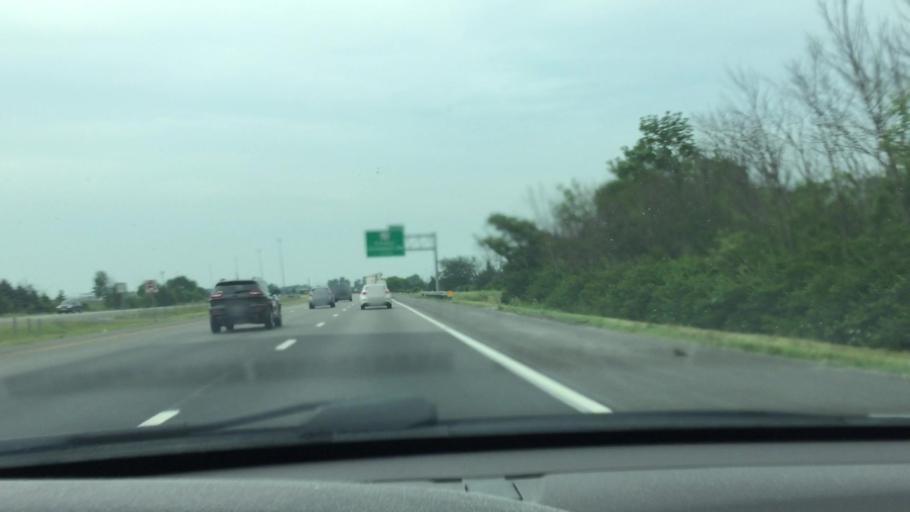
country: US
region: Ohio
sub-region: Franklin County
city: Grove City
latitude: 39.8331
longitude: -83.1020
